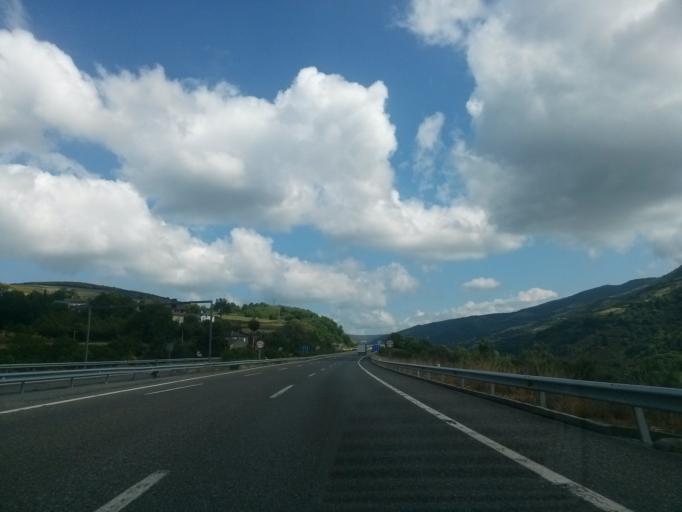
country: ES
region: Galicia
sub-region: Provincia de Lugo
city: San Roman
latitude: 42.7815
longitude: -7.1019
